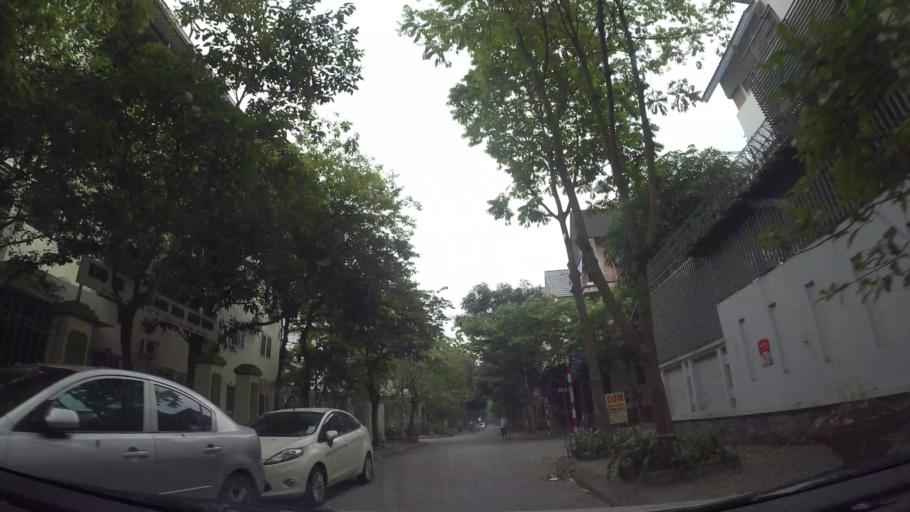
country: VN
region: Ha Noi
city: Cau Dien
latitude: 21.0314
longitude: 105.7635
